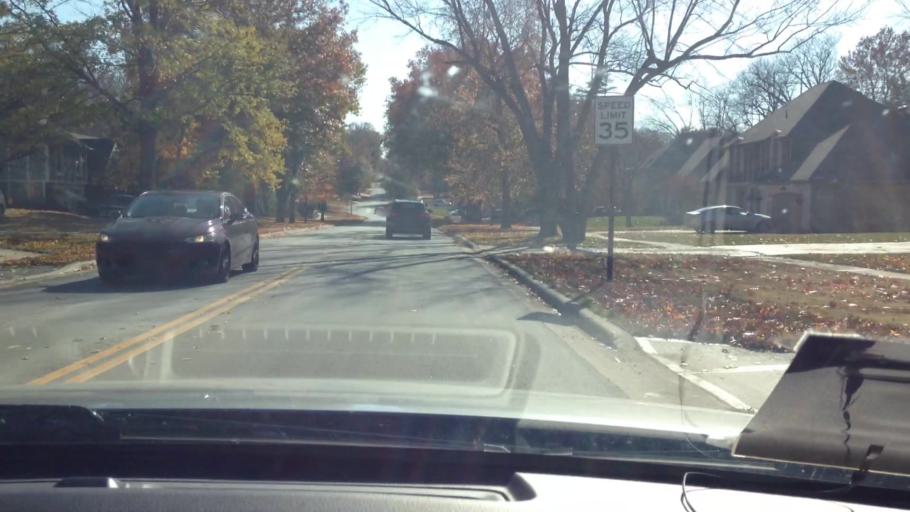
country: US
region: Kansas
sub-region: Johnson County
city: Leawood
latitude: 38.9492
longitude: -94.6391
